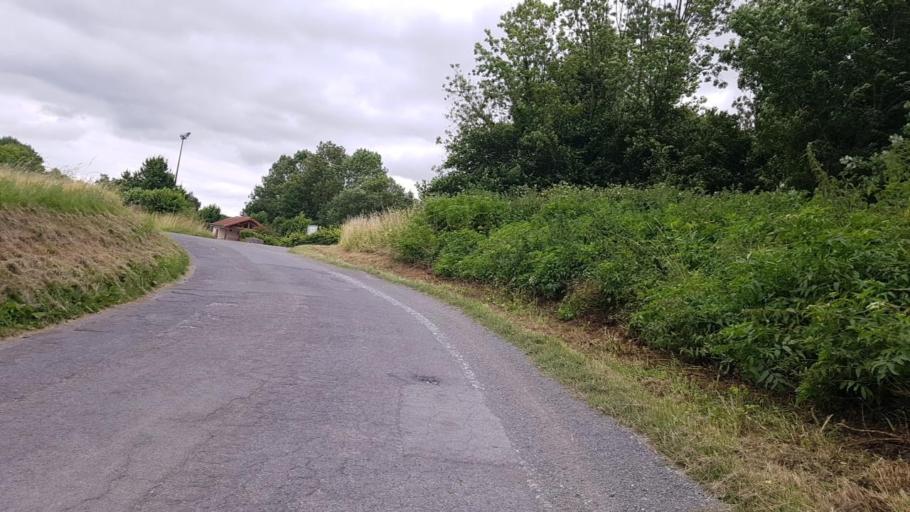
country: FR
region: Picardie
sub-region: Departement de l'Aisne
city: Guise
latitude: 49.8940
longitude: 3.6200
